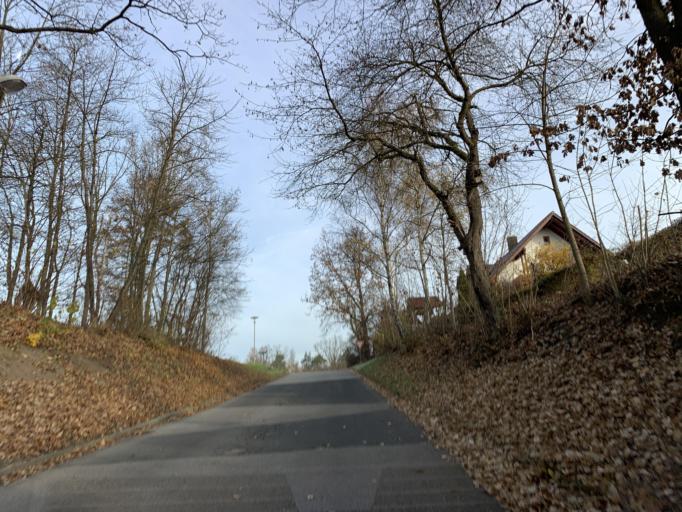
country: DE
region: Bavaria
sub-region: Upper Palatinate
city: Neunburg vorm Wald
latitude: 49.3559
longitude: 12.3842
